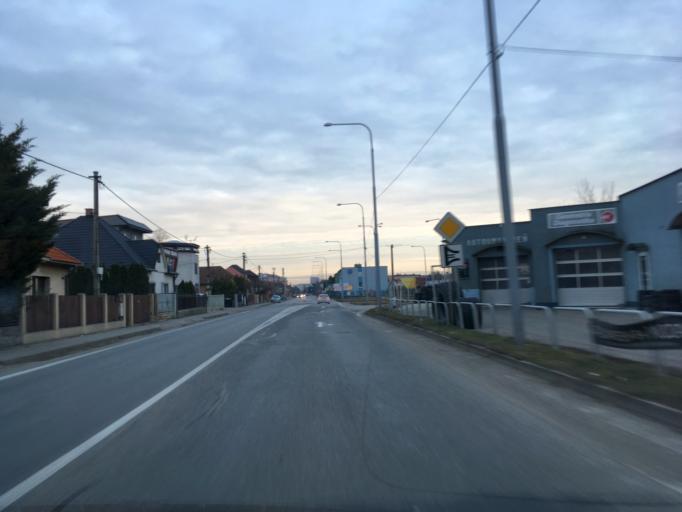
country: SK
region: Trnavsky
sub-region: Okres Dunajska Streda
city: Velky Meder
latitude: 47.8629
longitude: 17.7590
